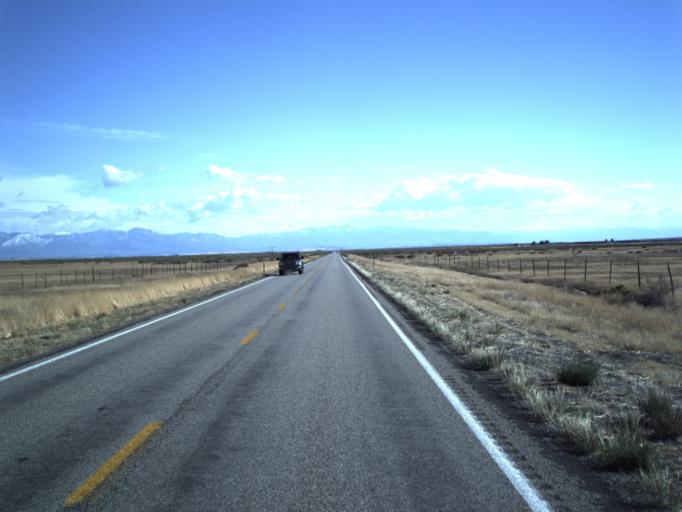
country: US
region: Utah
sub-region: Millard County
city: Delta
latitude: 39.3346
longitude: -112.4891
